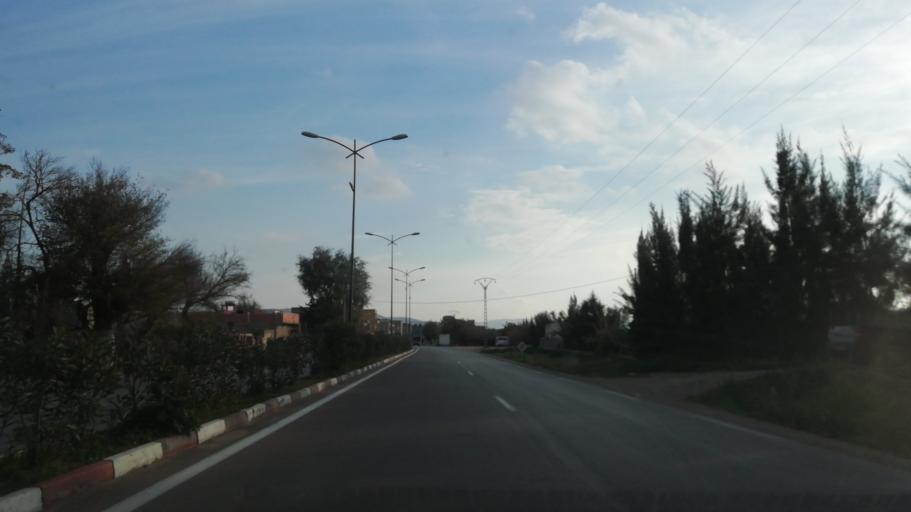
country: DZ
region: Mascara
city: Mascara
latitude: 35.6008
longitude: 0.0638
